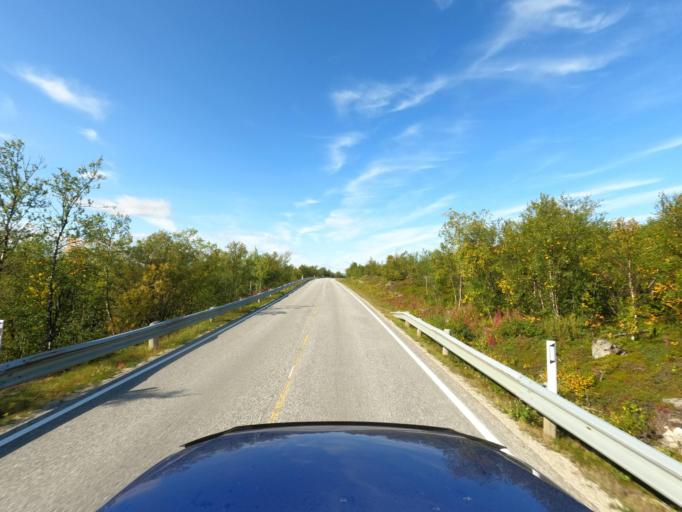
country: NO
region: Finnmark Fylke
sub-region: Porsanger
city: Lakselv
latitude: 69.7670
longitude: 25.1739
